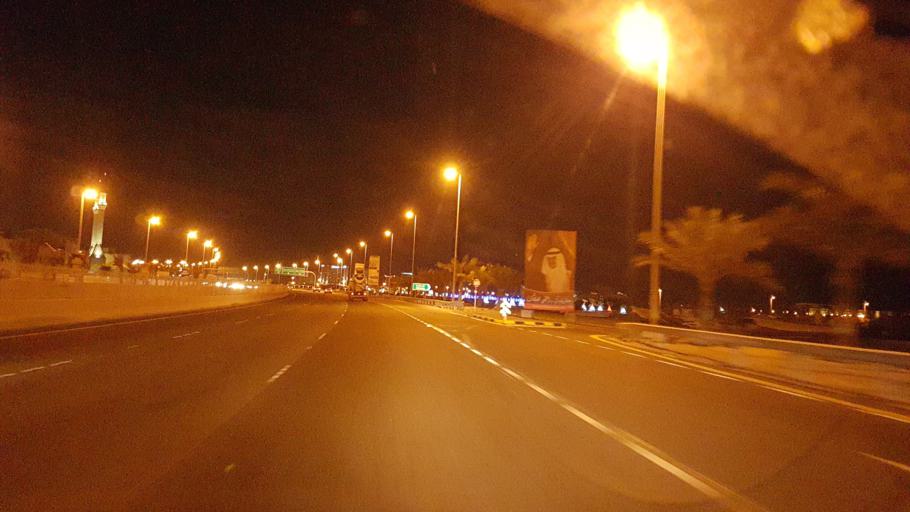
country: BH
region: Muharraq
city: Al Hadd
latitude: 26.2683
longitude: 50.6620
